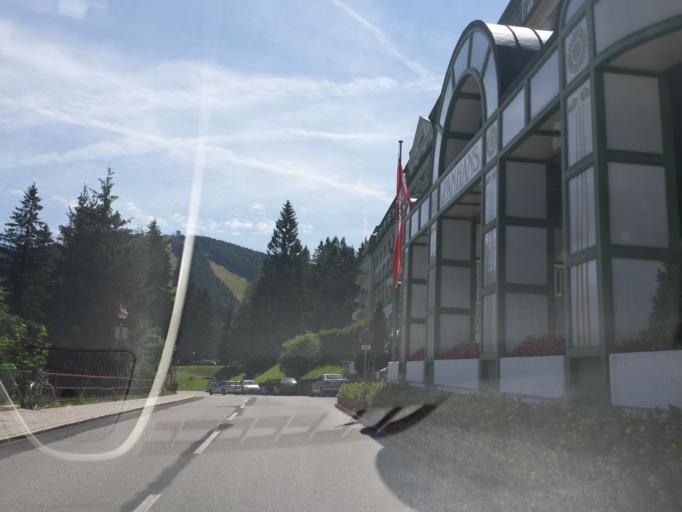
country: AT
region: Lower Austria
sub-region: Politischer Bezirk Neunkirchen
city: Semmering
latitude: 47.6370
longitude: 15.8257
